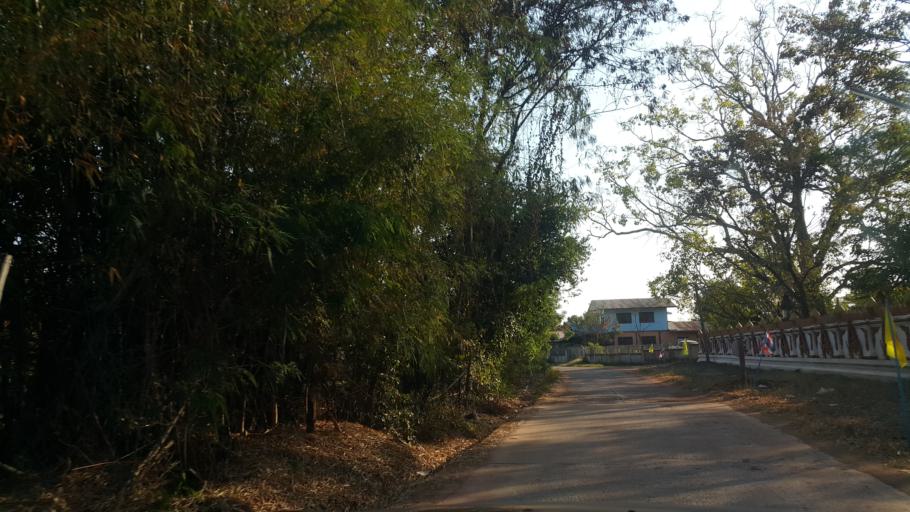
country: TH
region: Changwat Udon Thani
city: Ban Na Muang
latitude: 17.2221
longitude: 103.0765
